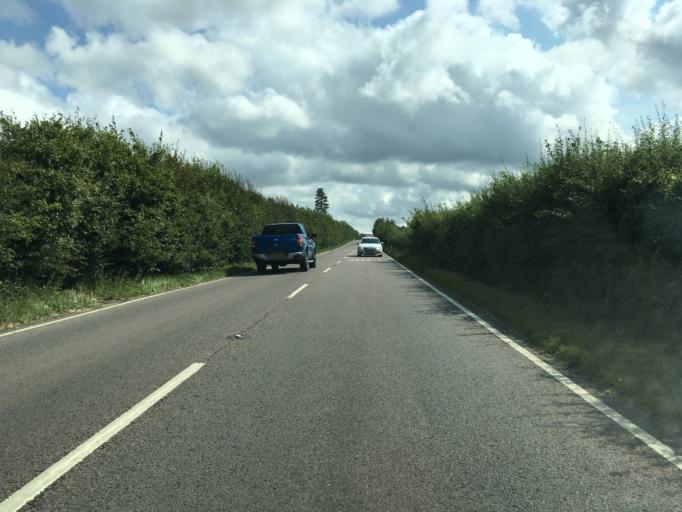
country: GB
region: England
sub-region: Kent
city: Headcorn
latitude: 51.1310
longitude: 0.6453
